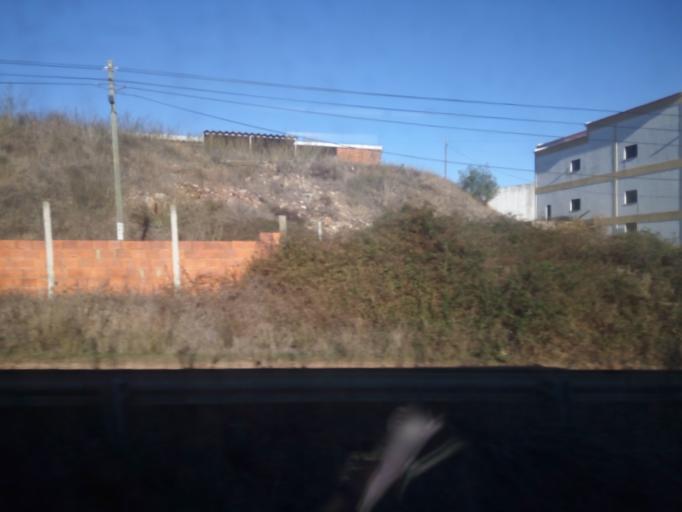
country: PT
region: Faro
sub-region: Silves
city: Sao Bartolomeu de Messines
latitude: 37.3447
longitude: -8.3587
